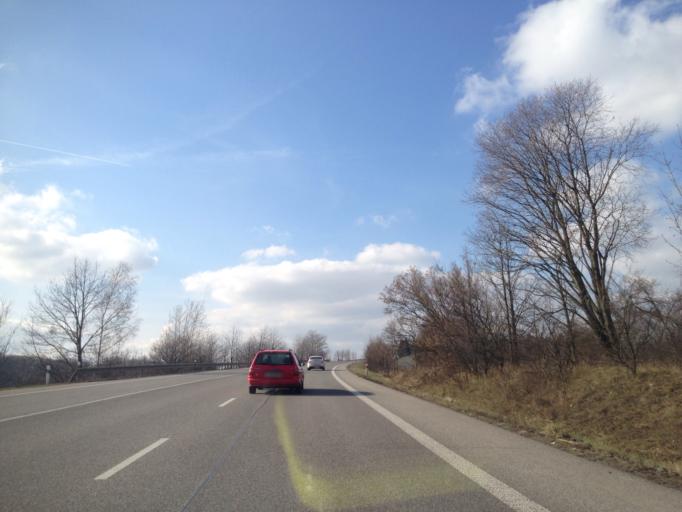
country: CZ
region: Kralovehradecky
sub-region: Okres Jicin
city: Sobotka
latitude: 50.4559
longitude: 15.2232
